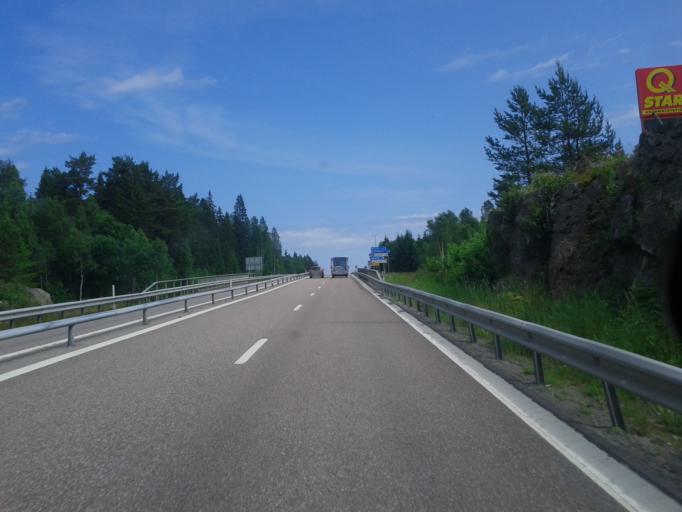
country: SE
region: Vaesternorrland
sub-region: OErnskoeldsviks Kommun
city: Husum
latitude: 63.3494
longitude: 19.1476
